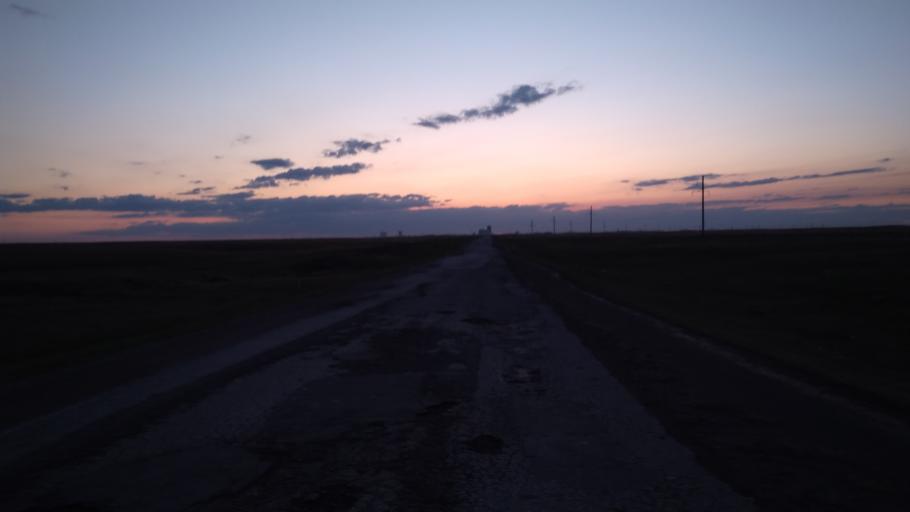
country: RU
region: Chelyabinsk
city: Troitsk
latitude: 54.0900
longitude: 61.6483
